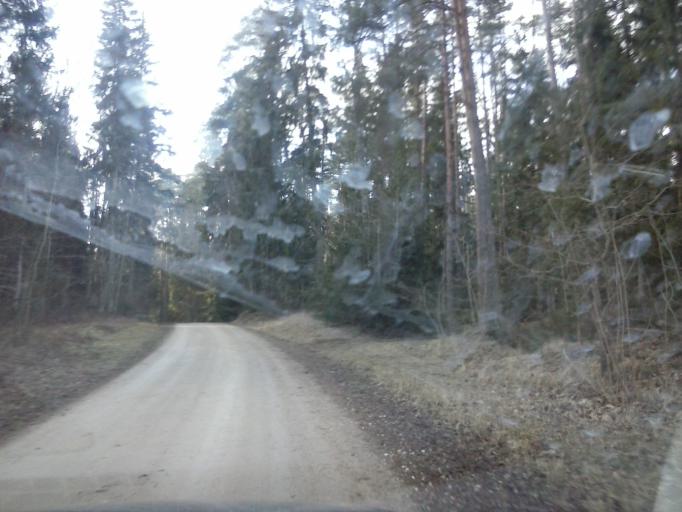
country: EE
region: Tartu
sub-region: Puhja vald
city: Puhja
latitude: 58.1611
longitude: 26.1553
